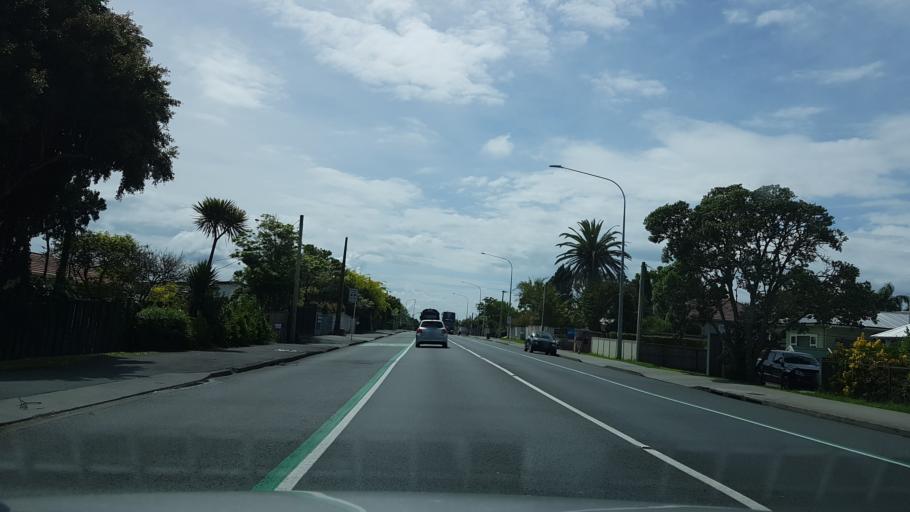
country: NZ
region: Auckland
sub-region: Auckland
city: North Shore
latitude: -36.8100
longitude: 174.7304
